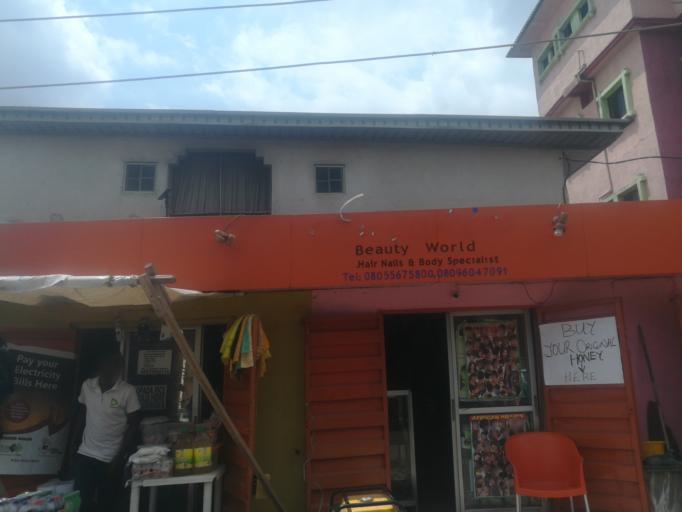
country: NG
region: Lagos
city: Somolu
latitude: 6.5593
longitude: 3.3859
